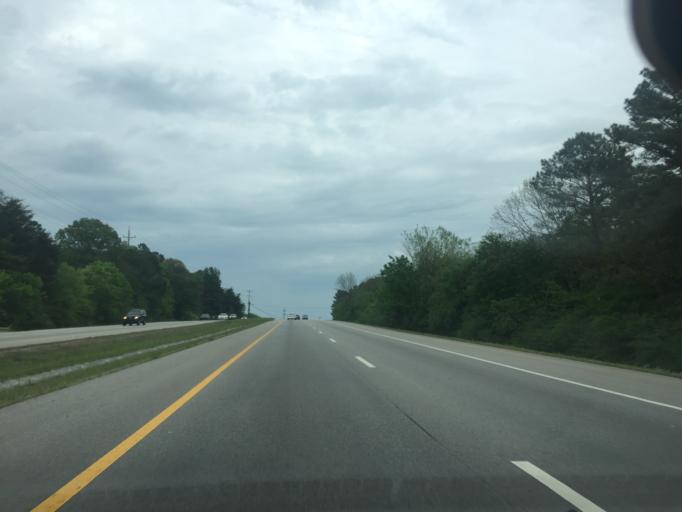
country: US
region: Tennessee
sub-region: Hamilton County
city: Harrison
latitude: 35.1010
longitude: -85.1680
